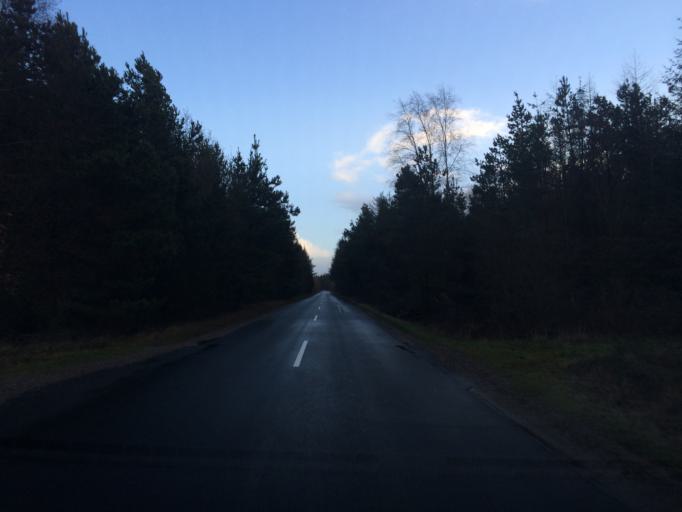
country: DK
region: Central Jutland
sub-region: Holstebro Kommune
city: Ulfborg
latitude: 56.2655
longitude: 8.3355
